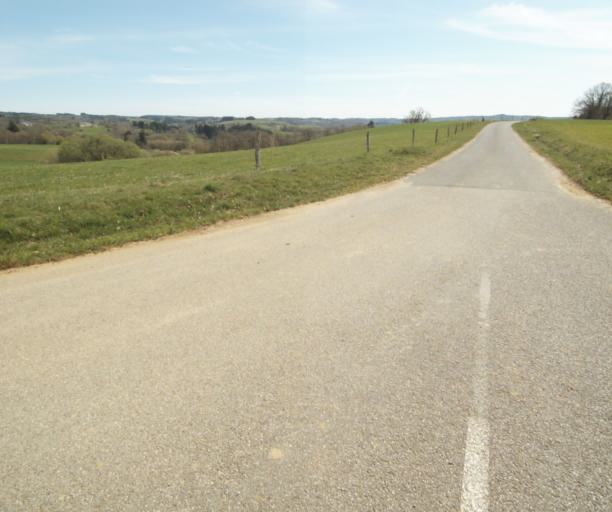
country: FR
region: Limousin
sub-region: Departement de la Correze
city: Correze
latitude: 45.3854
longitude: 1.8073
